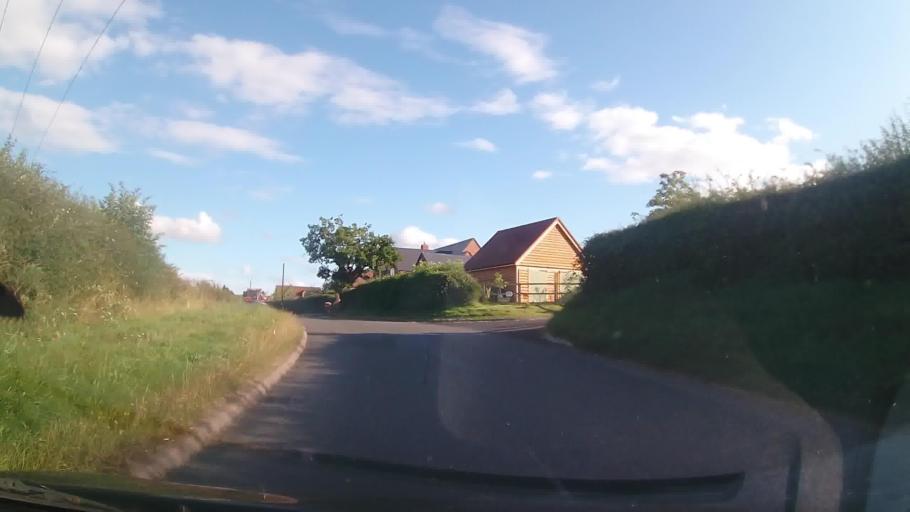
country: GB
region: England
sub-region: Shropshire
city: Great Hanwood
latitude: 52.6537
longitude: -2.8046
